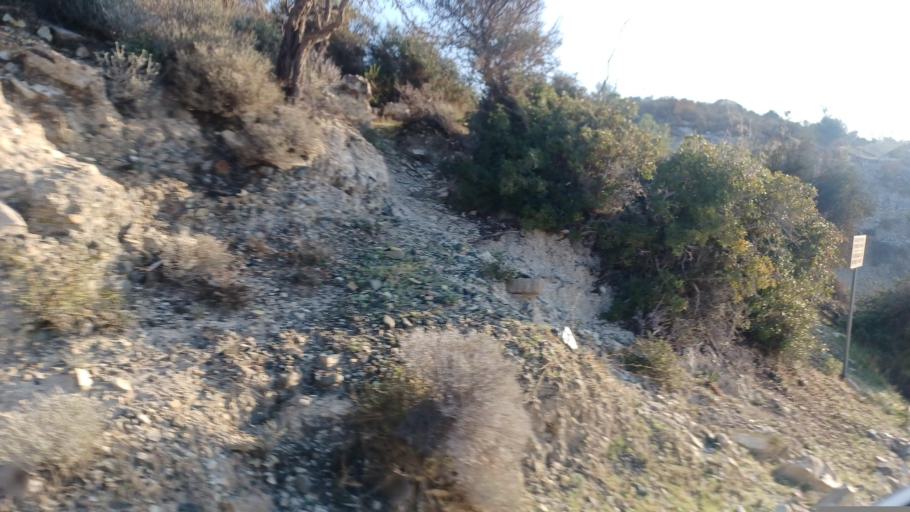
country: CY
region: Larnaka
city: Kofinou
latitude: 34.8179
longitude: 33.3170
